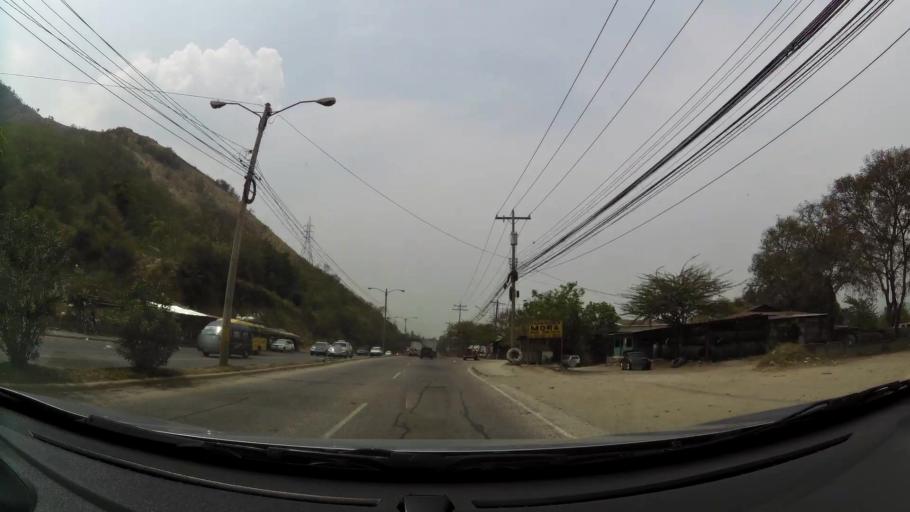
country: HN
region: Cortes
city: Chotepe
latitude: 15.4331
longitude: -88.0210
